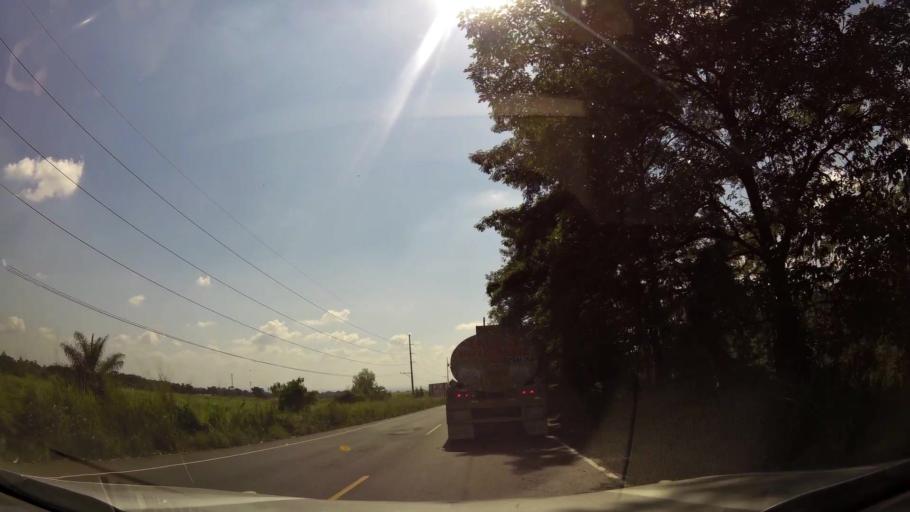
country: GT
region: Suchitepeque
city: Mazatenango
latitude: 14.5465
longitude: -91.5216
